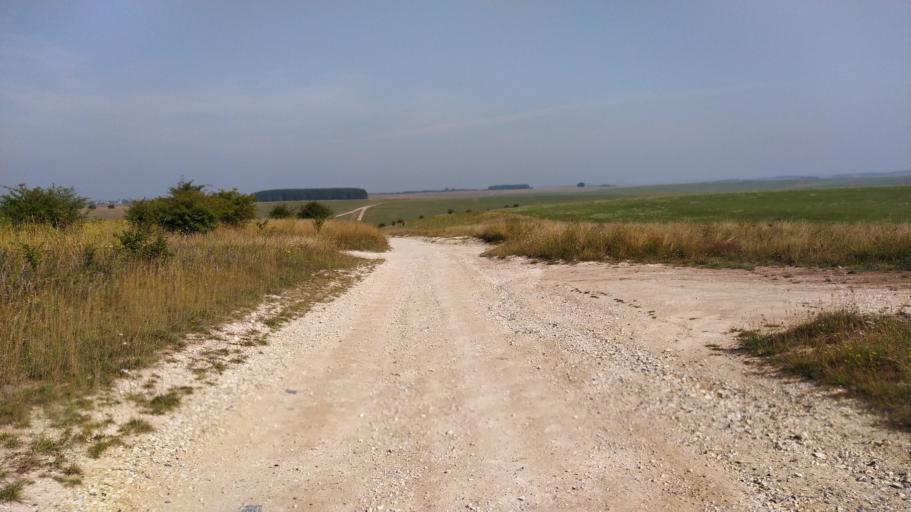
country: GB
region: England
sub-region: Wiltshire
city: Shrewton
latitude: 51.1883
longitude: -1.9534
